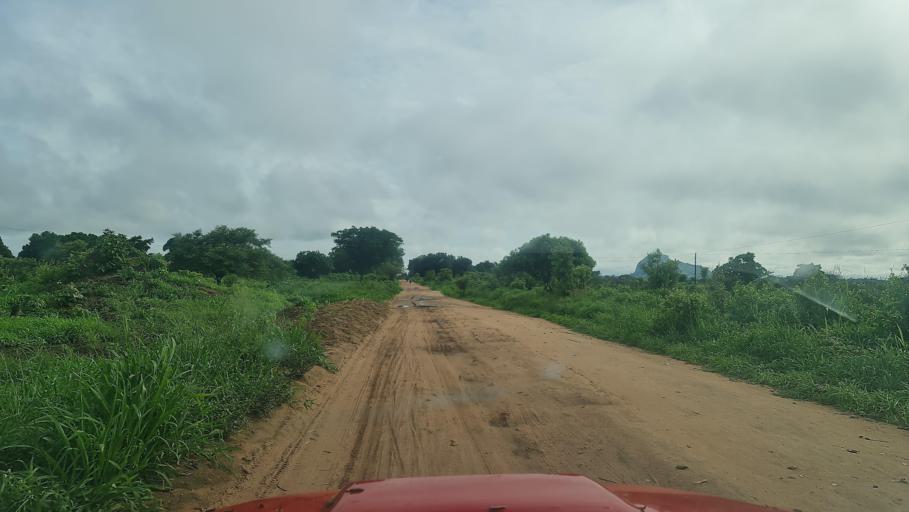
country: MW
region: Southern Region
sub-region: Nsanje District
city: Nsanje
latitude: -17.2850
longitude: 35.6101
